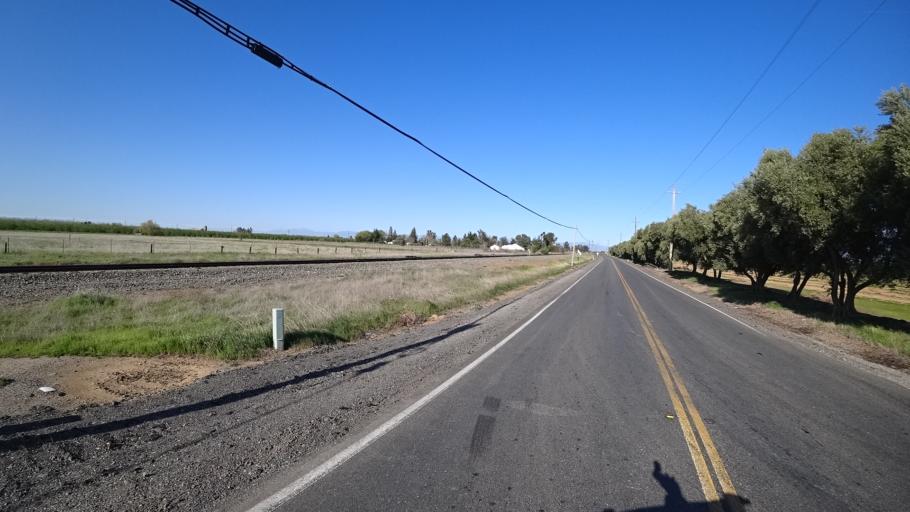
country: US
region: California
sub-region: Glenn County
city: Hamilton City
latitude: 39.7680
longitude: -122.1044
